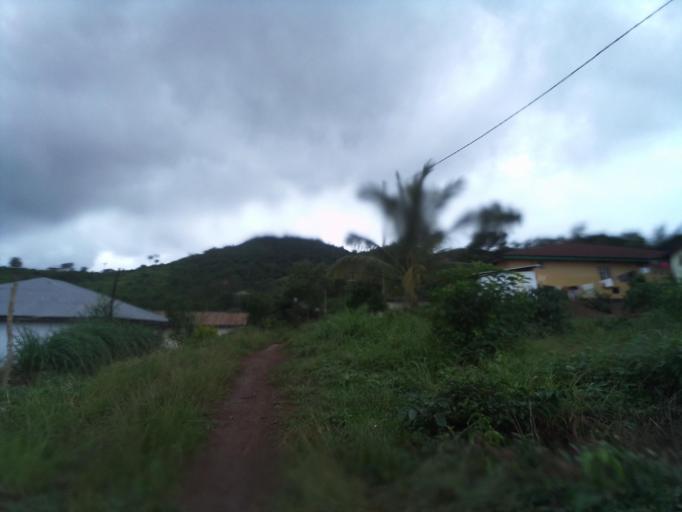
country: SL
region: Eastern Province
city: Kenema
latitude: 7.8479
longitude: -11.1857
